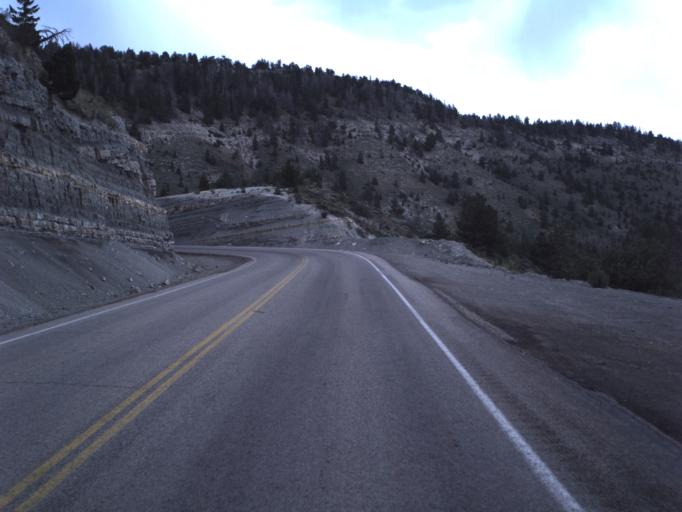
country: US
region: Utah
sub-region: Carbon County
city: Helper
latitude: 39.8671
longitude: -110.7651
